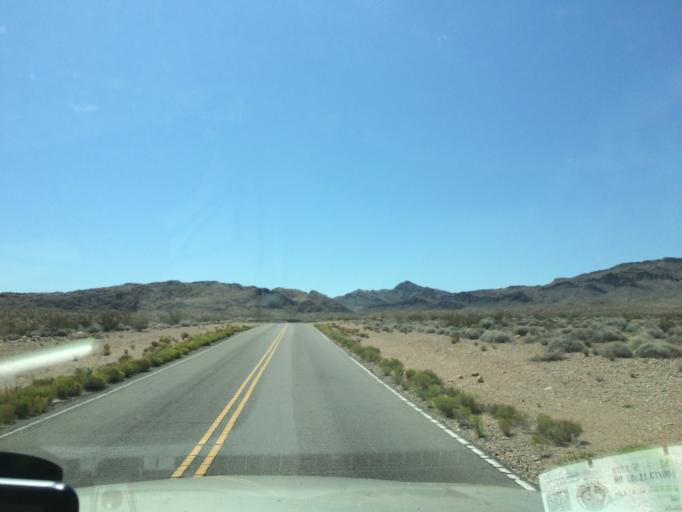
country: US
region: Nevada
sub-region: Clark County
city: Moapa Valley
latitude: 36.4356
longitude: -114.6390
